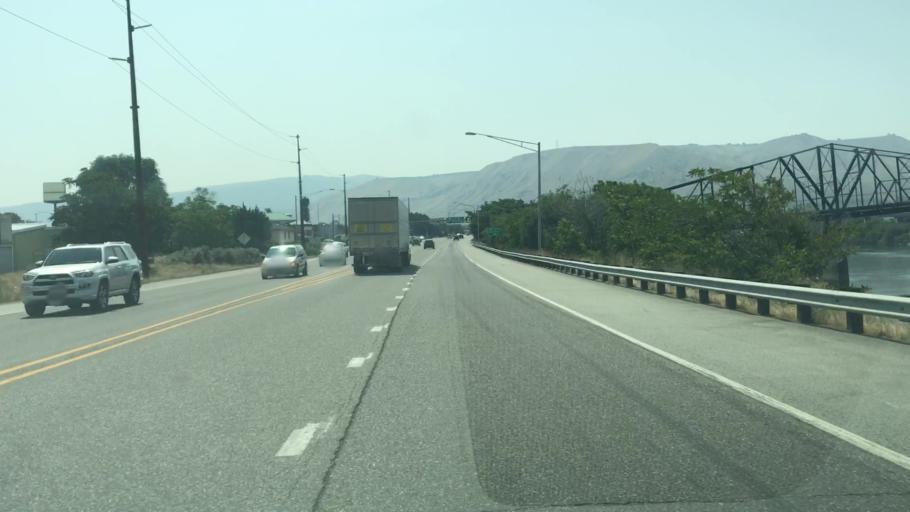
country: US
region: Washington
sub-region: Douglas County
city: East Wenatchee
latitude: 47.4173
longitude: -120.2957
